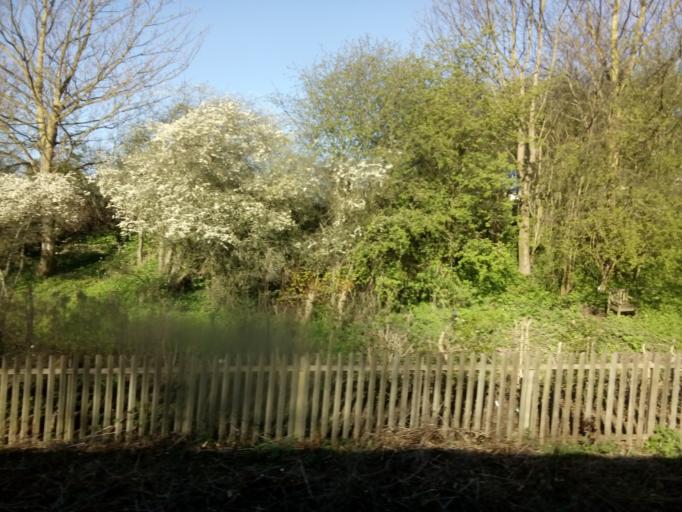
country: GB
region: England
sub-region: Northumberland
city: Morpeth
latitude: 55.1595
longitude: -1.6865
